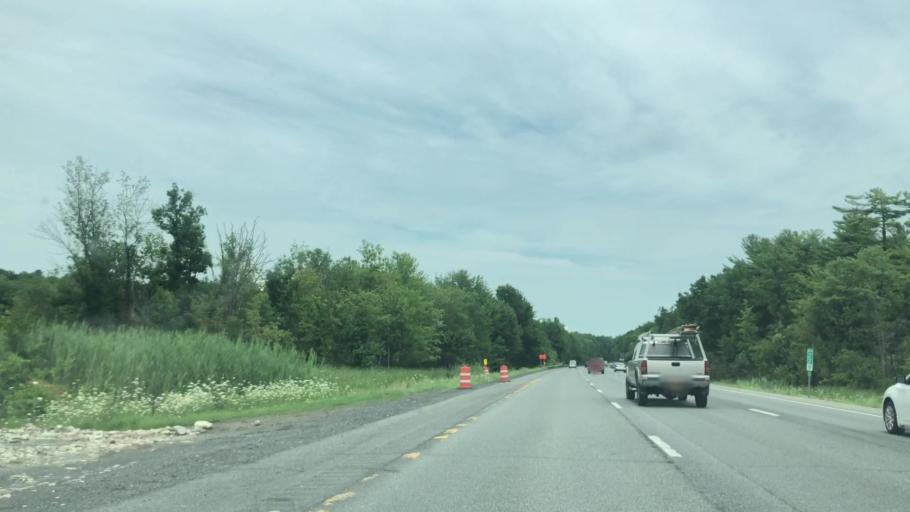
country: US
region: New York
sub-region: Saratoga County
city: Ballston Spa
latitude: 42.9958
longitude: -73.8033
